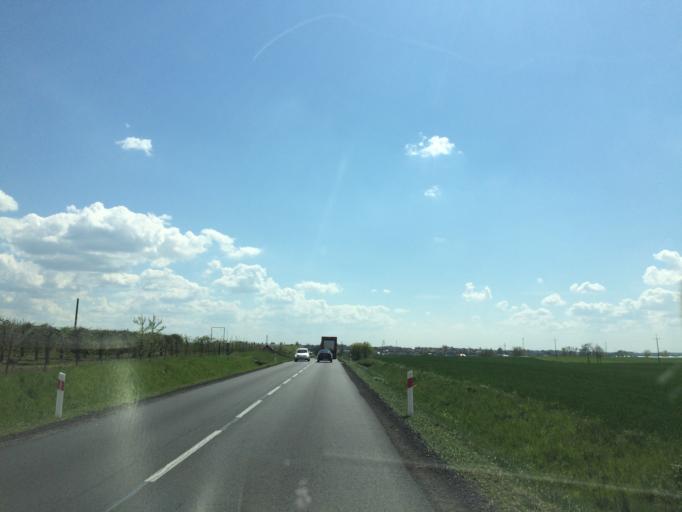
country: PL
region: Warmian-Masurian Voivodeship
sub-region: Powiat ilawski
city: Lubawa
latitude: 53.5228
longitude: 19.7470
